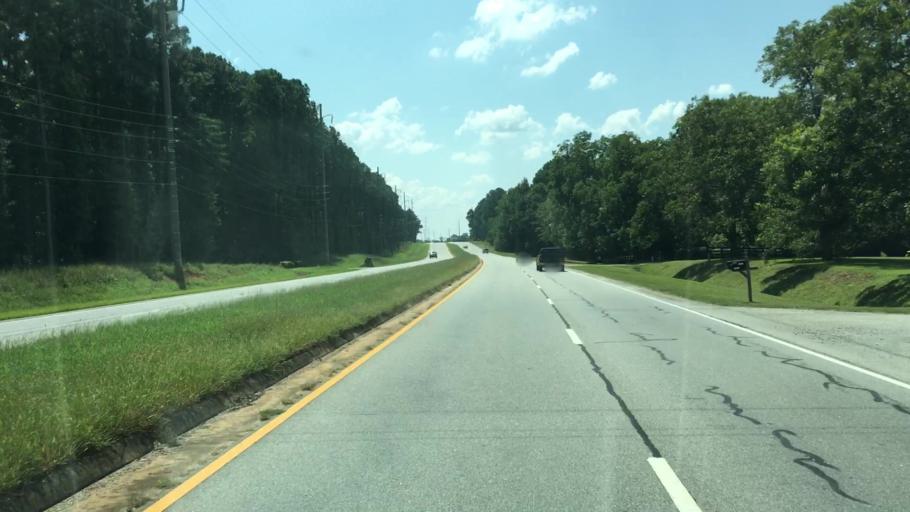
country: US
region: Georgia
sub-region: Morgan County
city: Madison
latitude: 33.5745
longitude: -83.4559
